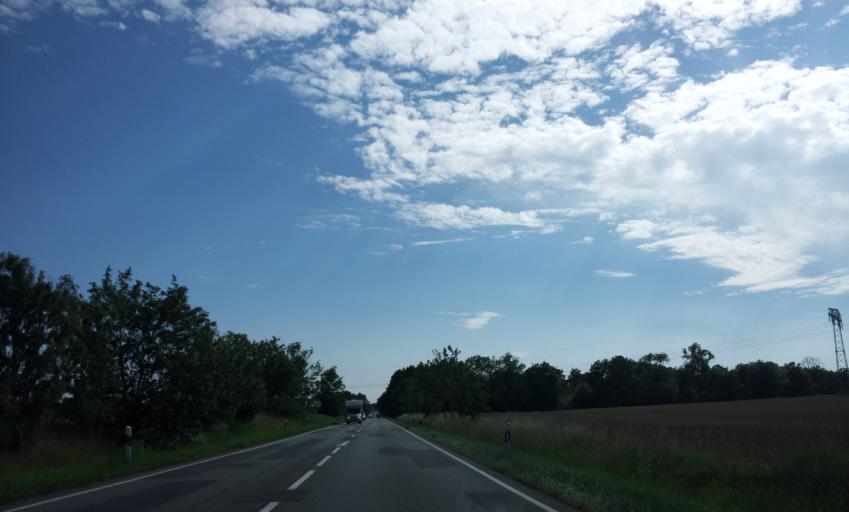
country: DE
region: Mecklenburg-Vorpommern
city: Bergen auf Ruegen
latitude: 54.4180
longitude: 13.4034
